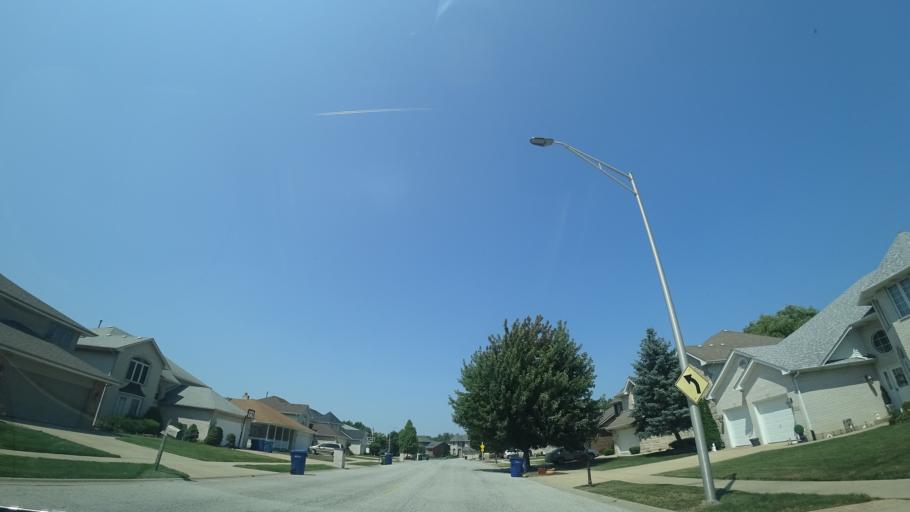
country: US
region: Illinois
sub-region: Cook County
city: Oak Lawn
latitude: 41.6951
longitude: -87.7514
